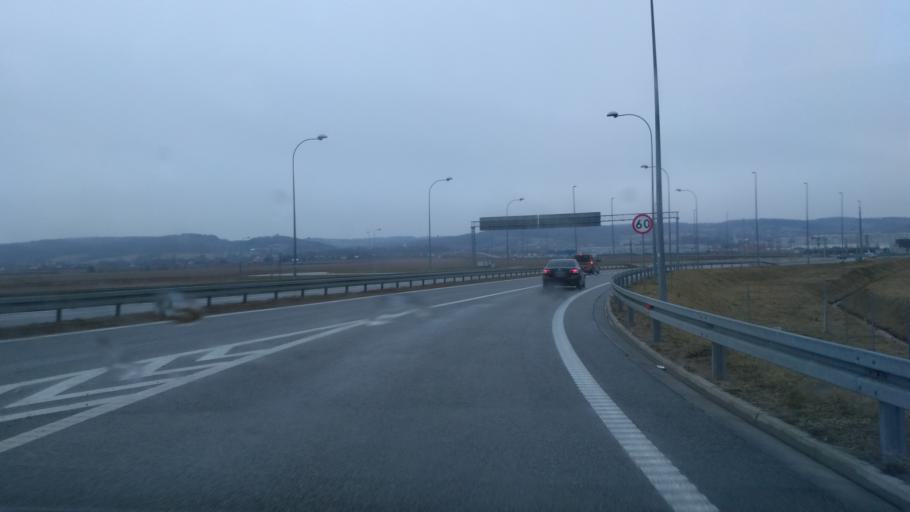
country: PL
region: Subcarpathian Voivodeship
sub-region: Powiat debicki
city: Brzeznica
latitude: 50.0787
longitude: 21.4701
